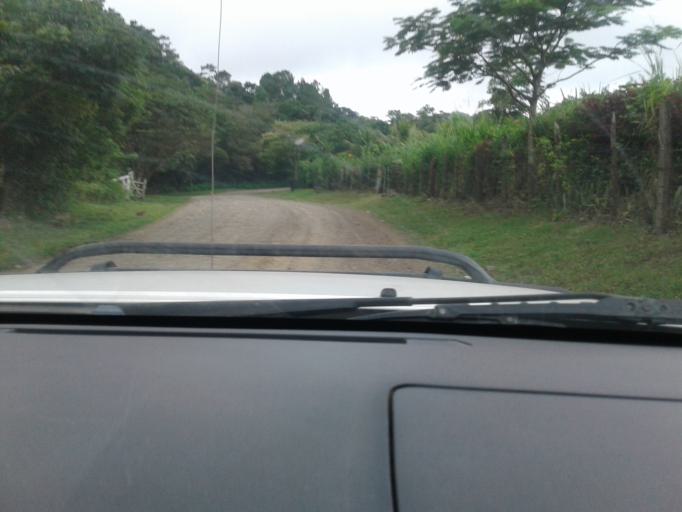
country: NI
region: Matagalpa
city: San Ramon
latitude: 12.9153
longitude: -85.7876
